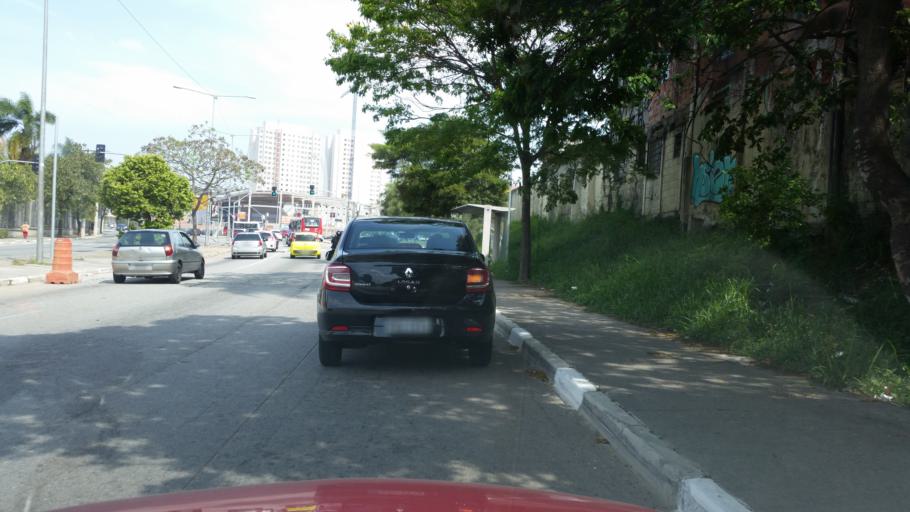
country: BR
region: Sao Paulo
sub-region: Ferraz De Vasconcelos
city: Ferraz de Vasconcelos
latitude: -23.5340
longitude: -46.4293
